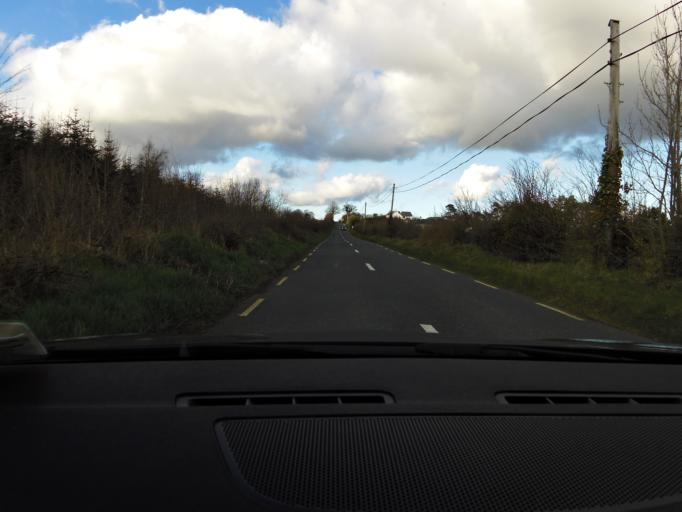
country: IE
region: Connaught
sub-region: Roscommon
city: Castlerea
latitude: 53.6791
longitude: -8.4893
